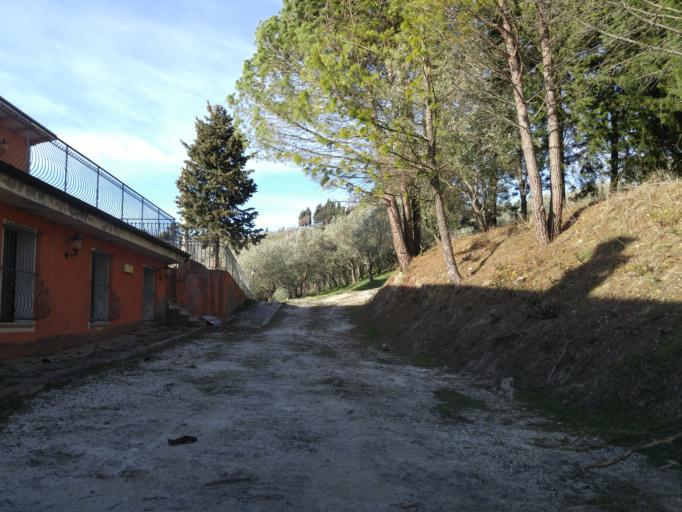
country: IT
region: The Marches
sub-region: Provincia di Pesaro e Urbino
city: Cartoceto
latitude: 43.7615
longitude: 12.8760
